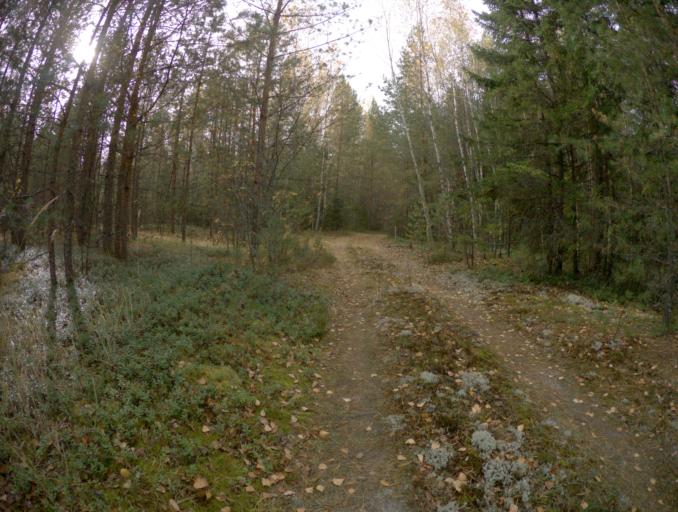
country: RU
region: Vladimir
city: Vorsha
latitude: 55.9657
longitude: 40.1398
